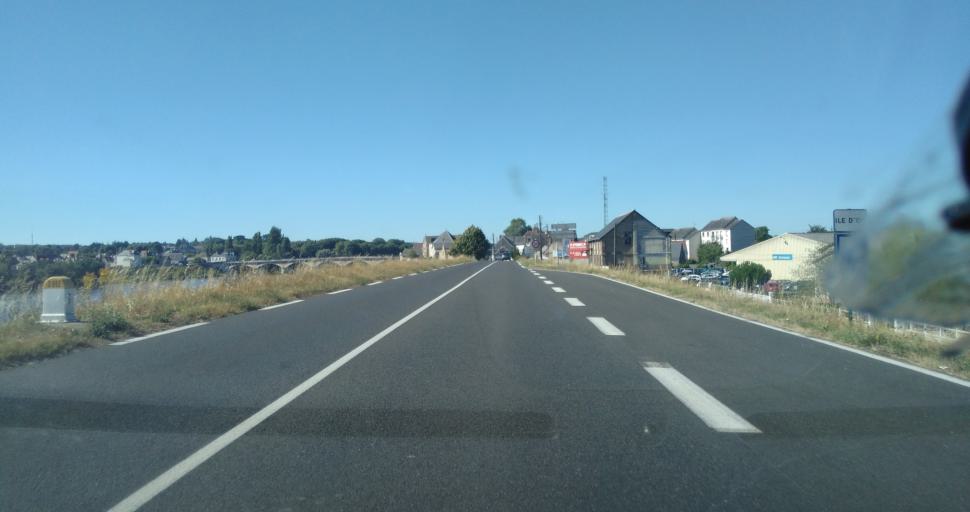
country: FR
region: Centre
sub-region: Departement d'Indre-et-Loire
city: Amboise
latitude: 47.4210
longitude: 0.9864
